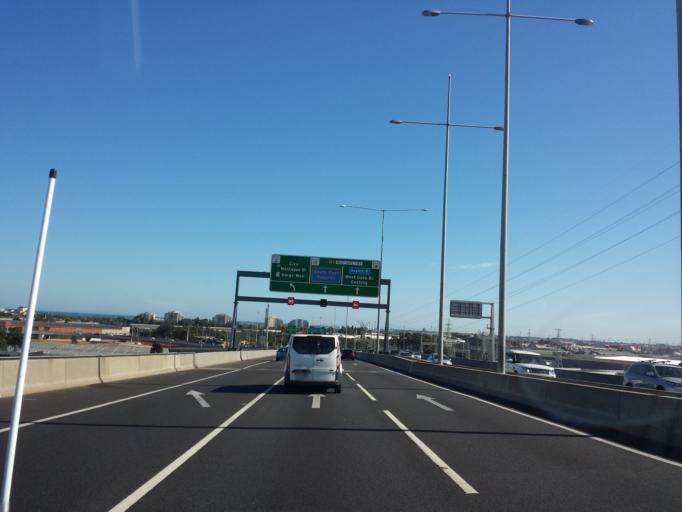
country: AU
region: Victoria
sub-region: Melbourne
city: Docklands
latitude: -37.8212
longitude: 144.9317
